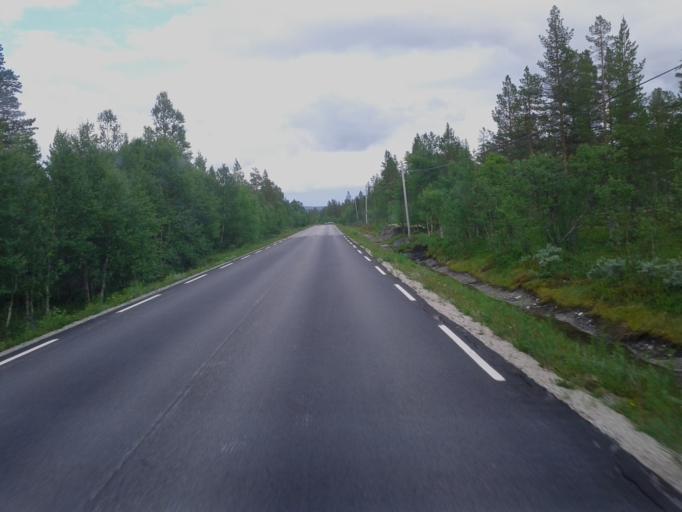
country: NO
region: Sor-Trondelag
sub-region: Roros
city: Roros
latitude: 62.3107
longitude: 11.6743
